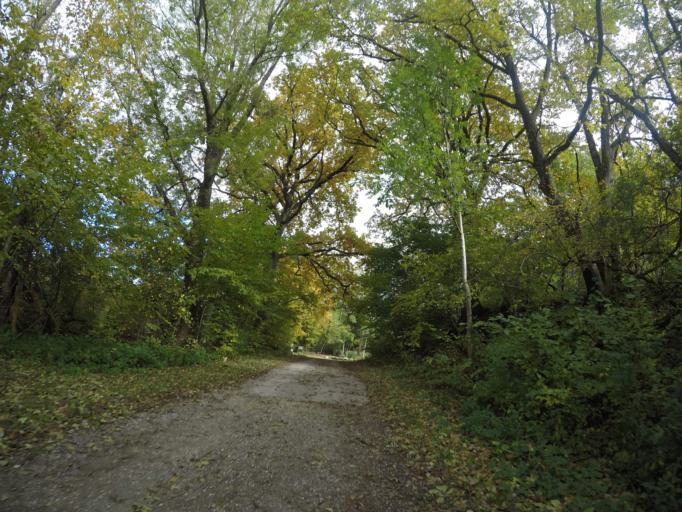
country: DE
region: Baden-Wuerttemberg
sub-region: Tuebingen Region
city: Tiefenbach
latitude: 48.0834
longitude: 9.6479
